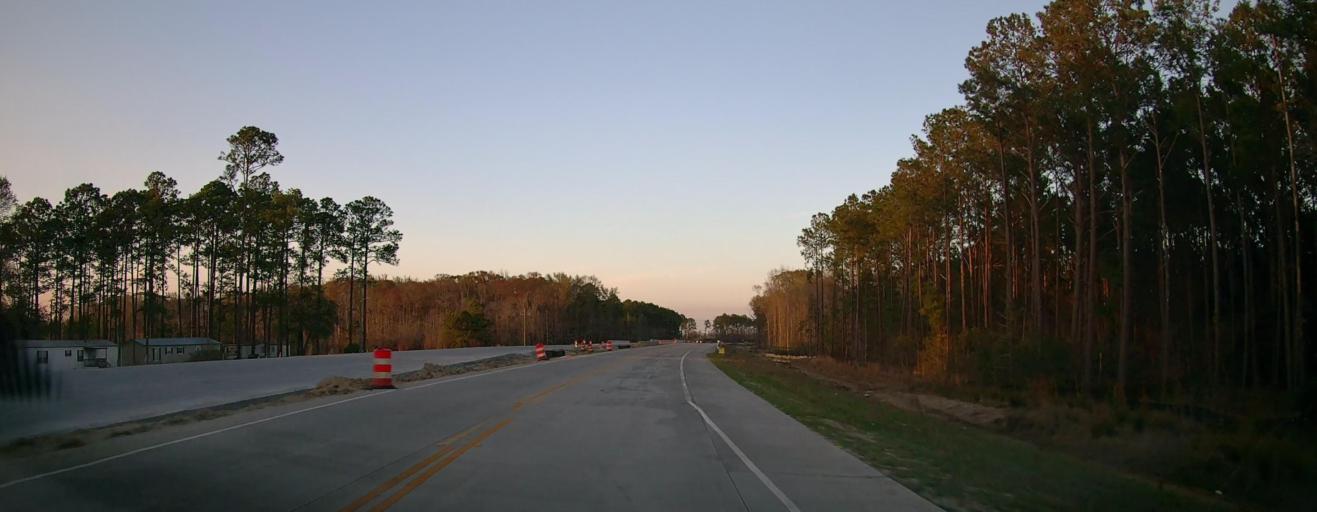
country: US
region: Georgia
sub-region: Chatham County
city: Bloomingdale
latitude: 32.1066
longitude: -81.3235
